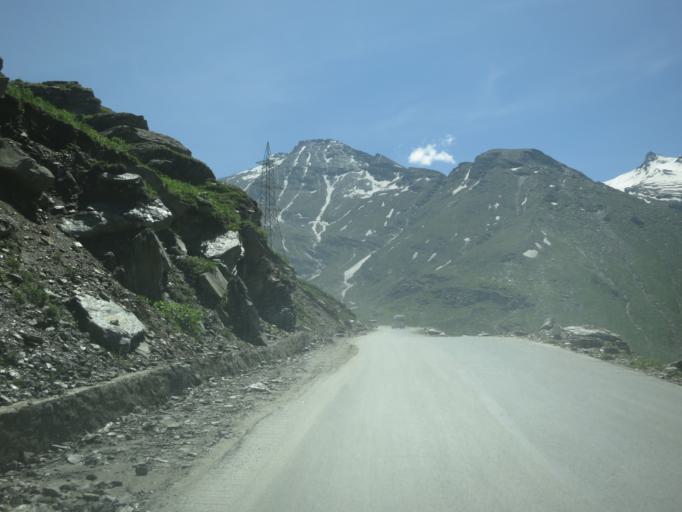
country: IN
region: Himachal Pradesh
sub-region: Kulu
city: Manali
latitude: 32.3546
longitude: 77.2211
